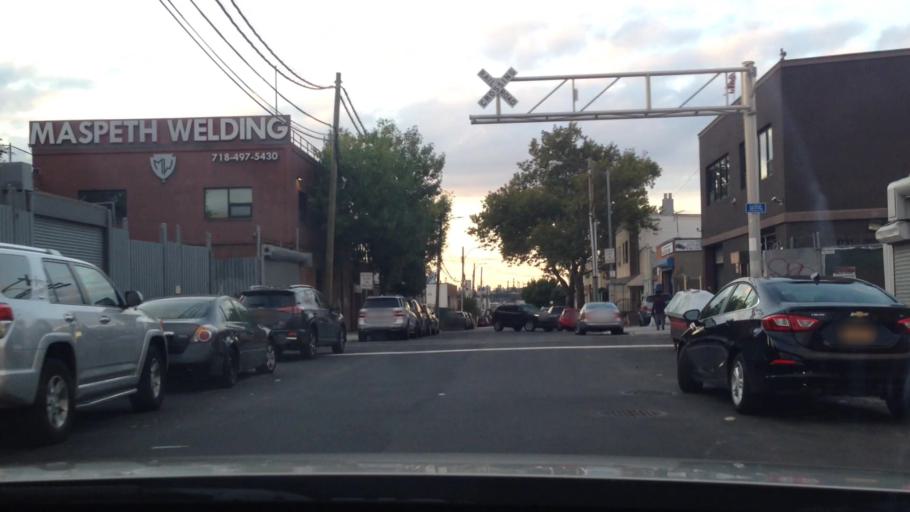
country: US
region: New York
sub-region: Queens County
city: Long Island City
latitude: 40.7160
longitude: -73.9138
